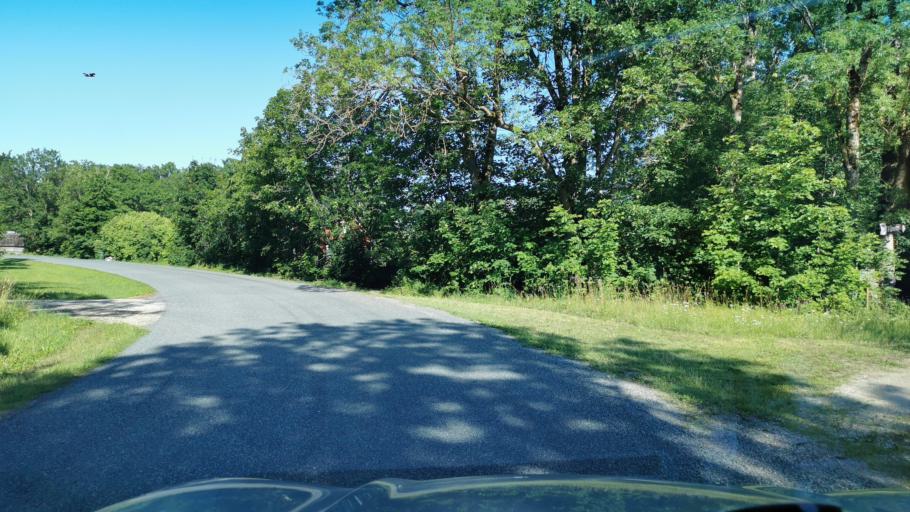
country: EE
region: Harju
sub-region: Paldiski linn
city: Paldiski
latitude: 59.2080
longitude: 24.0099
